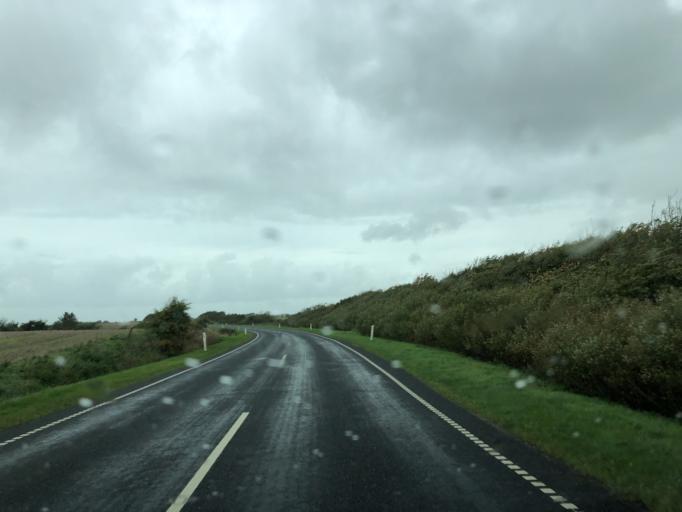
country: DK
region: North Denmark
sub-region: Thisted Kommune
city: Hurup
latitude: 56.7338
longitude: 8.3379
